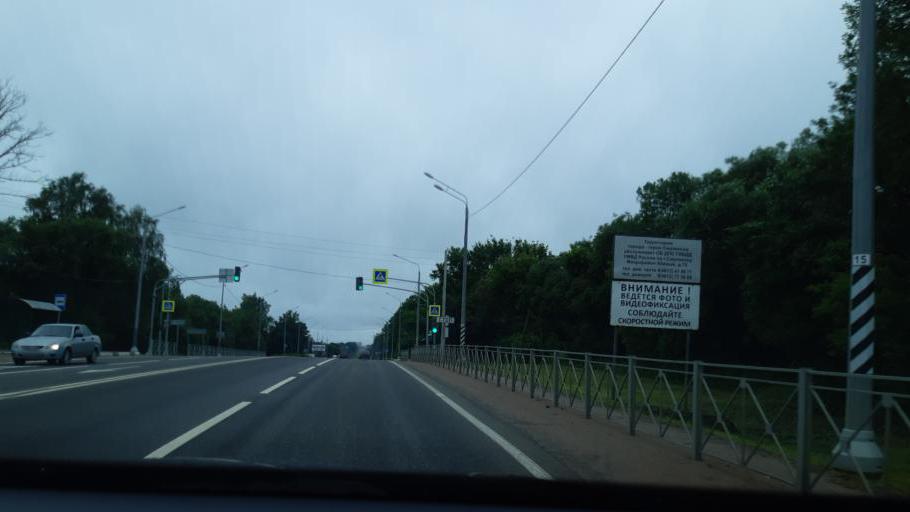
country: RU
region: Smolensk
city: Smolensk
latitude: 54.7161
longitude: 32.1082
